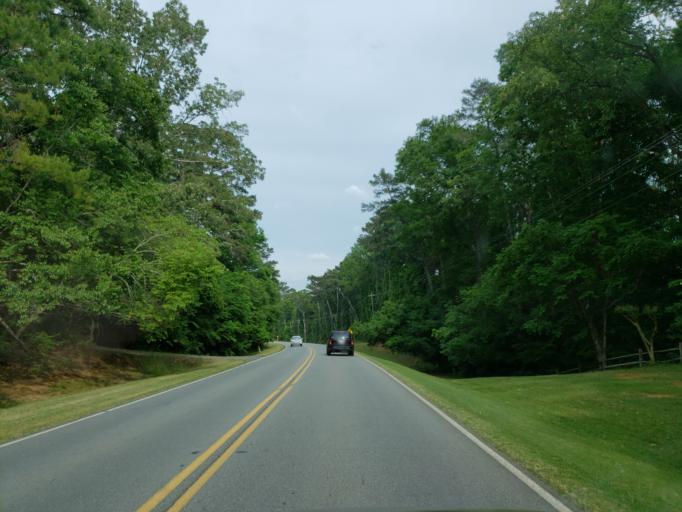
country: US
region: Georgia
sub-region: Dooly County
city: Vienna
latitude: 32.1109
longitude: -83.8418
